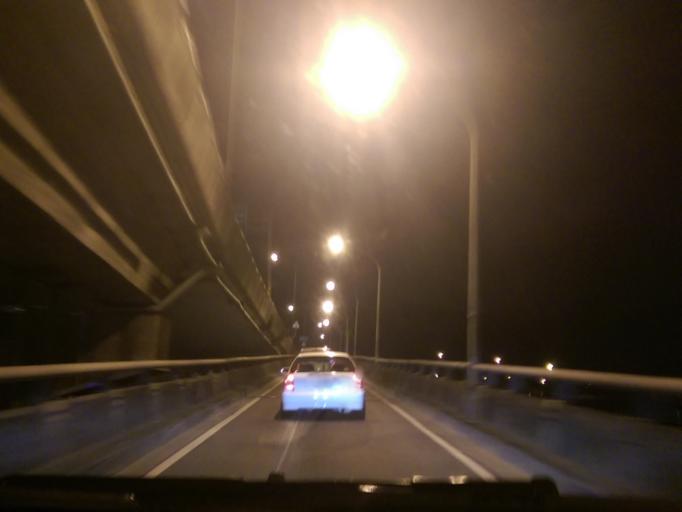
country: TW
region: Taipei
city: Taipei
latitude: 25.0468
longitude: 121.5033
